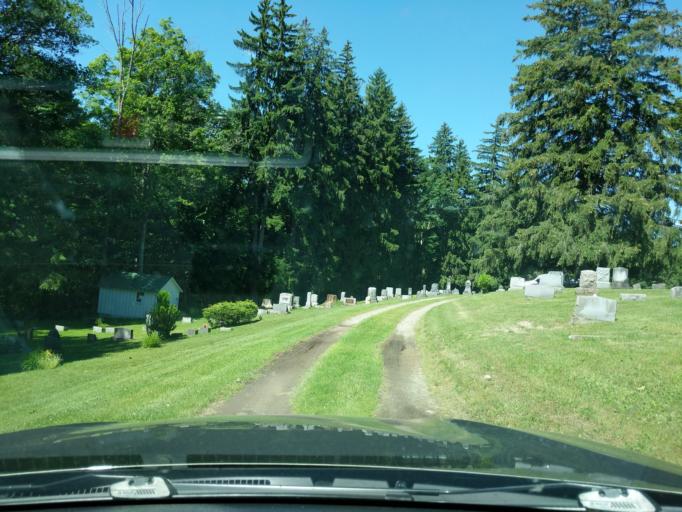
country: US
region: New York
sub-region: Tompkins County
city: East Ithaca
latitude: 42.3831
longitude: -76.3857
